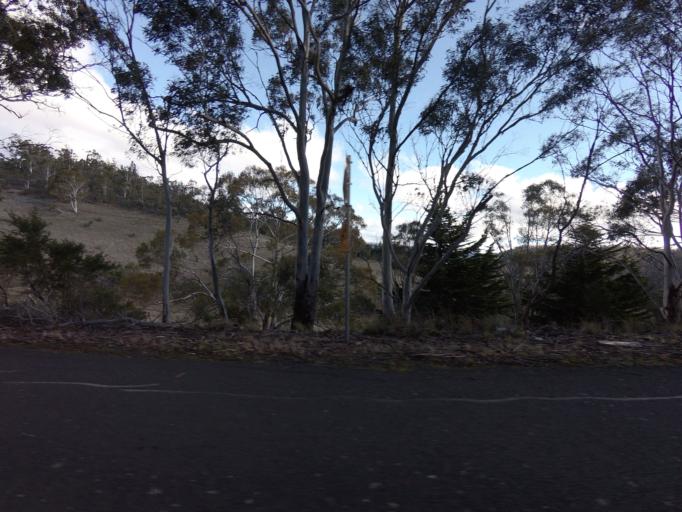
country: AU
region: Tasmania
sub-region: Derwent Valley
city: New Norfolk
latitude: -42.7343
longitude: 147.0326
